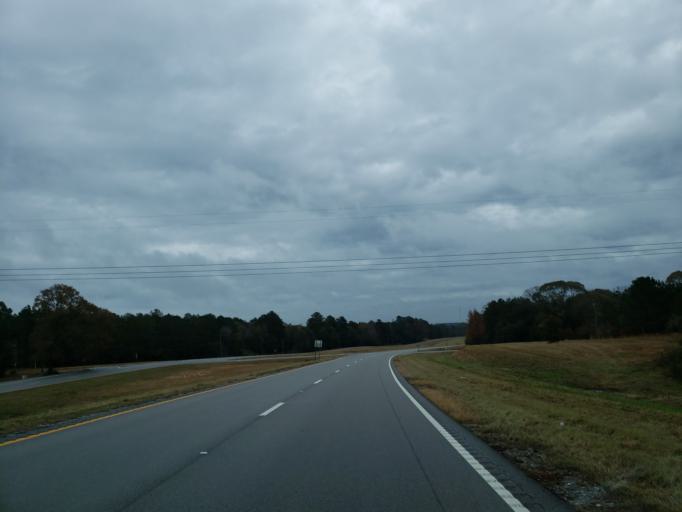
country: US
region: Mississippi
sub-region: Wayne County
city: Waynesboro
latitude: 31.6960
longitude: -88.7249
